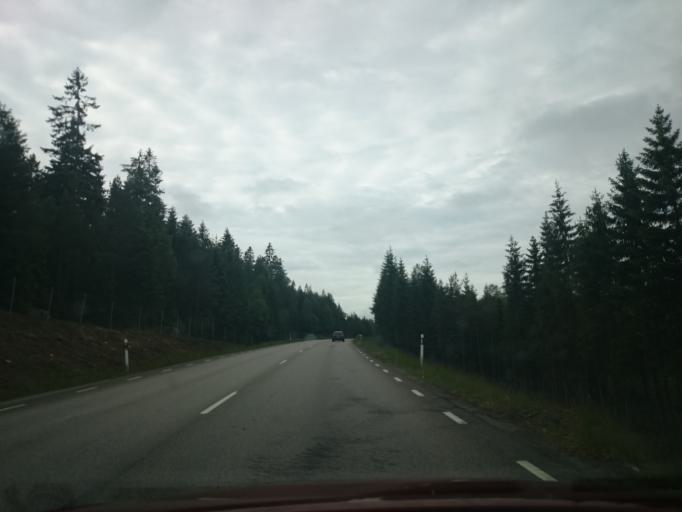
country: SE
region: Vaestra Goetaland
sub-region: Harryda Kommun
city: Hindas
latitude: 57.6884
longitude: 12.3710
